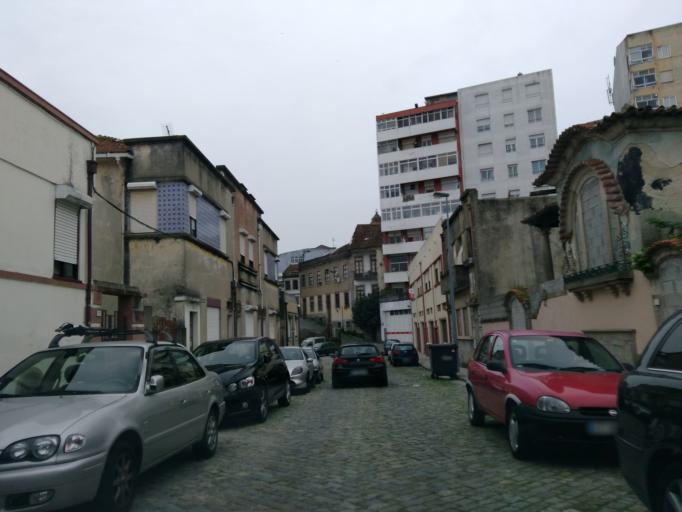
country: PT
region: Porto
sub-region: Porto
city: Porto
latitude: 41.1509
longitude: -8.5904
